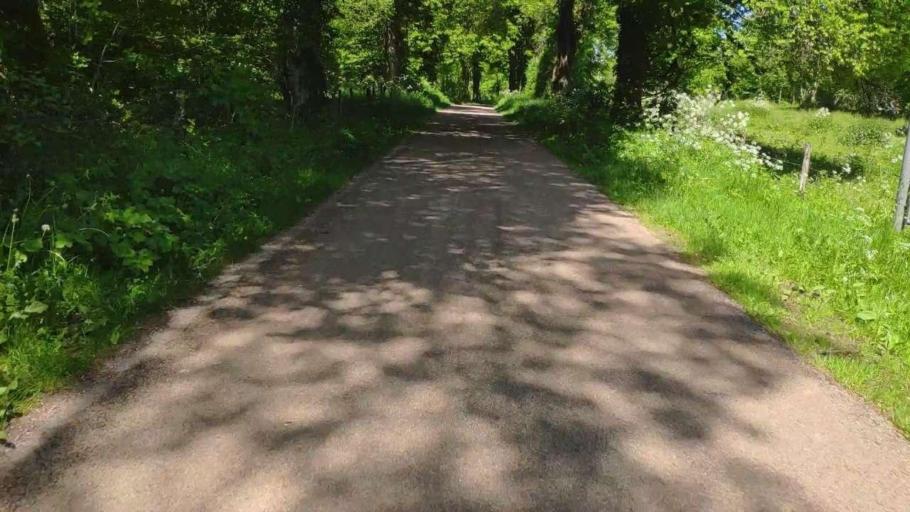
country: FR
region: Franche-Comte
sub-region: Departement du Jura
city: Poligny
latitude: 46.7316
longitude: 5.7369
